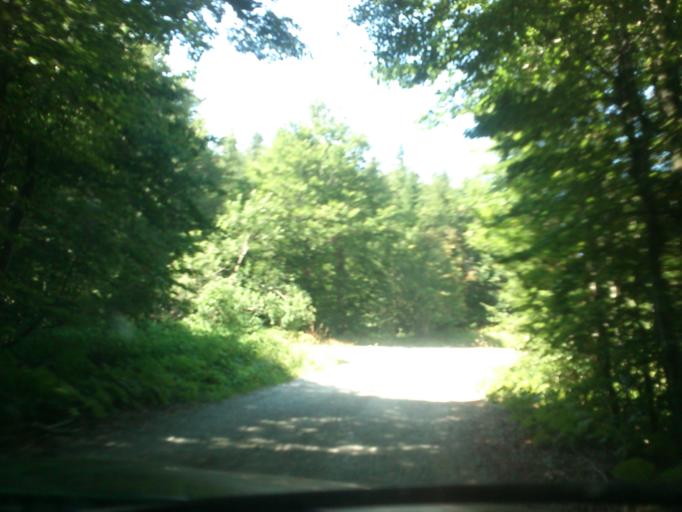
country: HR
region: Licko-Senjska
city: Senj
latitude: 44.8211
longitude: 14.9786
